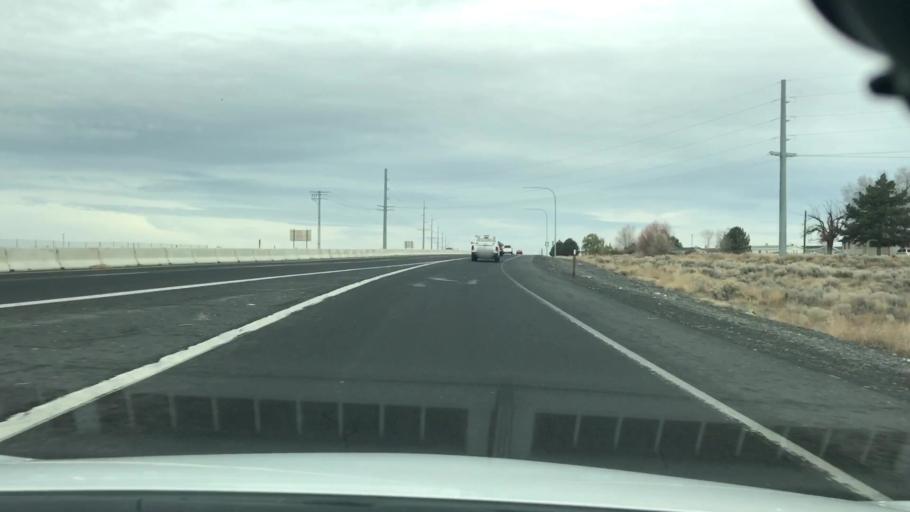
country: US
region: Washington
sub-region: Grant County
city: Moses Lake
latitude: 47.1446
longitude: -119.2825
